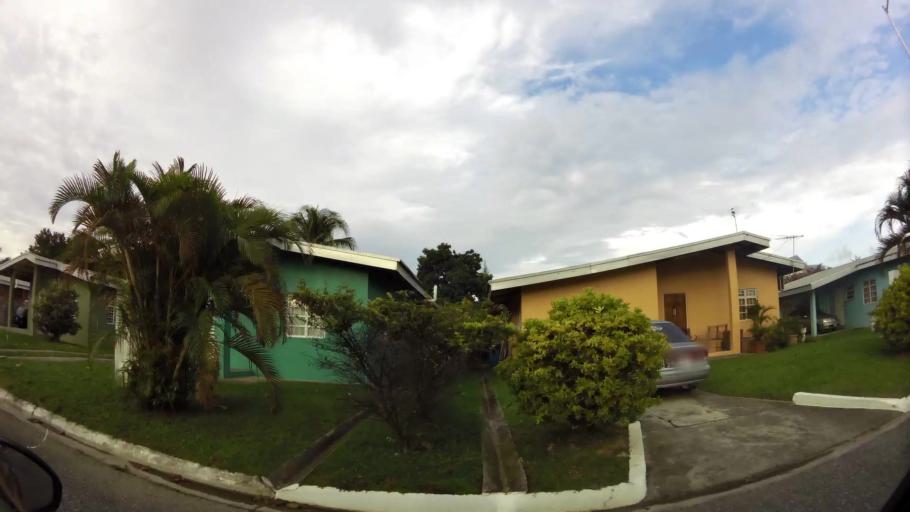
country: TT
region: Tunapuna/Piarco
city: Tunapuna
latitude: 10.6389
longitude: -61.4141
